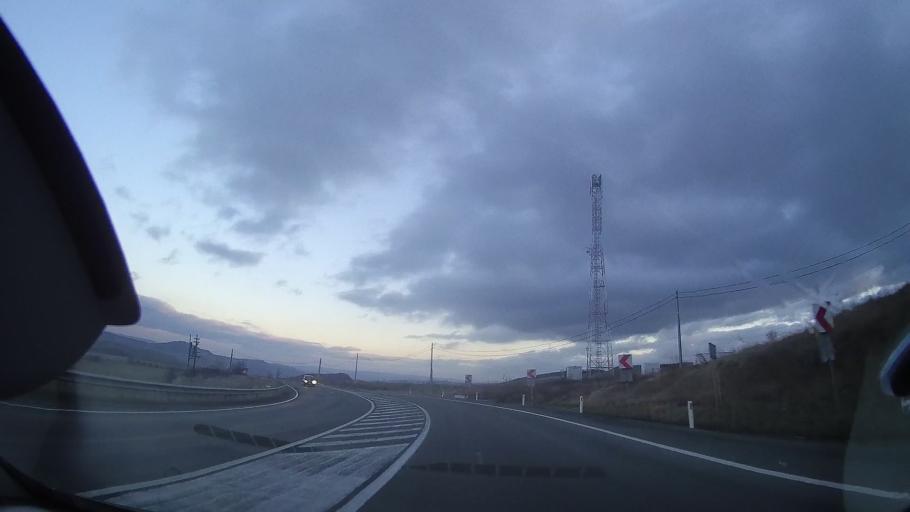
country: RO
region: Cluj
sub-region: Comuna Aghiresu
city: Aghiresu
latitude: 46.8198
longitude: 23.2062
